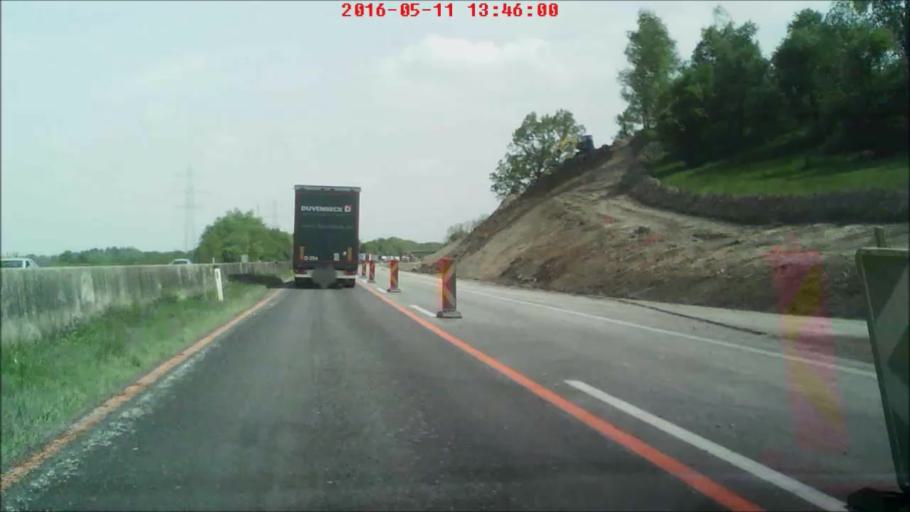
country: AT
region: Upper Austria
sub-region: Politischer Bezirk Vocklabruck
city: Wolfsegg am Hausruck
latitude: 48.2134
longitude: 13.6273
